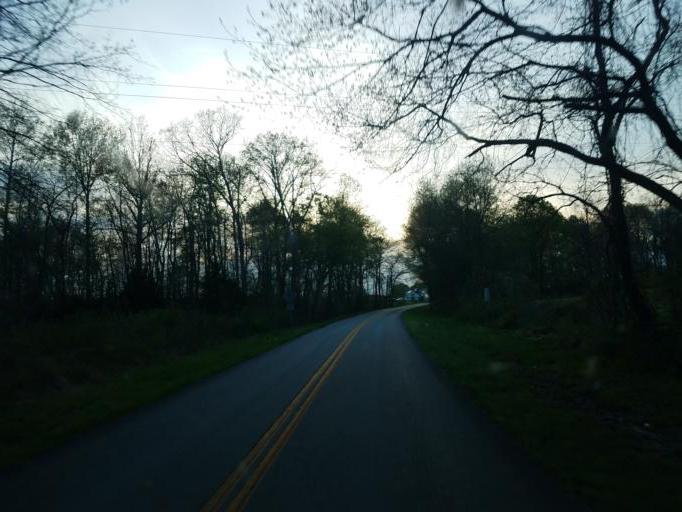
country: US
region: Kentucky
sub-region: Hart County
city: Munfordville
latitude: 37.2364
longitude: -85.7147
